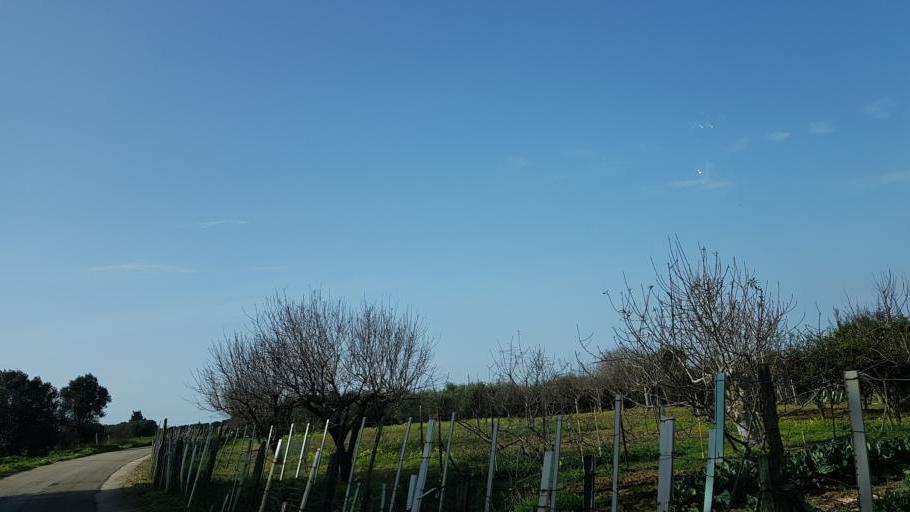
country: IT
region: Apulia
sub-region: Provincia di Brindisi
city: Brindisi
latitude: 40.6207
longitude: 17.8946
